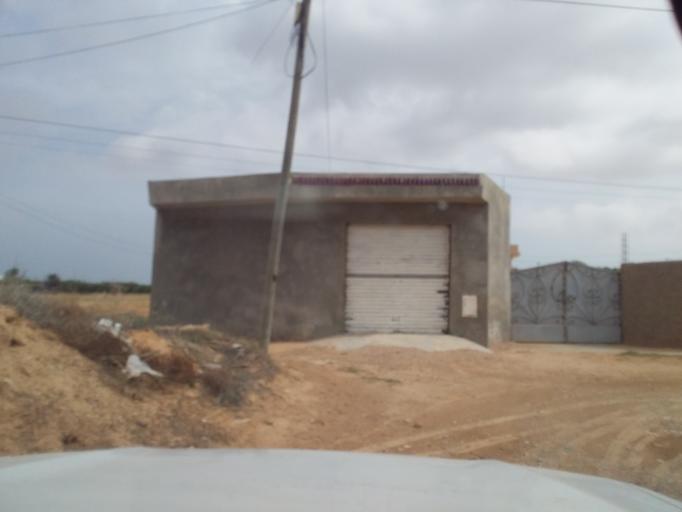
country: TN
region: Qabis
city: Gabes
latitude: 33.6293
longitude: 10.3094
